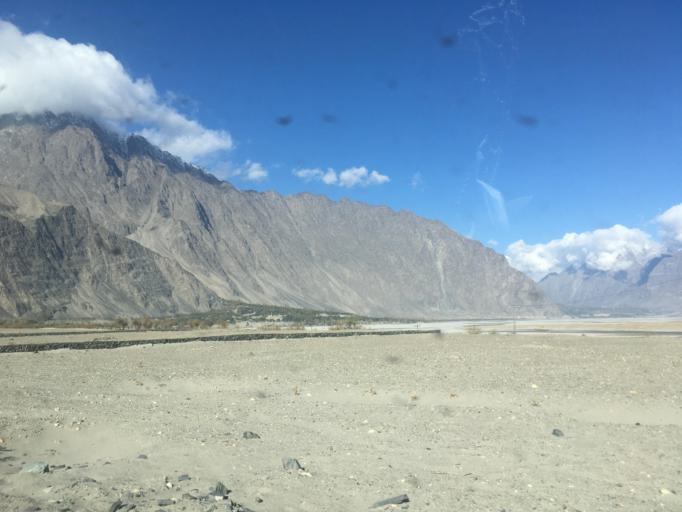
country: PK
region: Gilgit-Baltistan
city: Skardu
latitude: 35.3596
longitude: 75.5314
